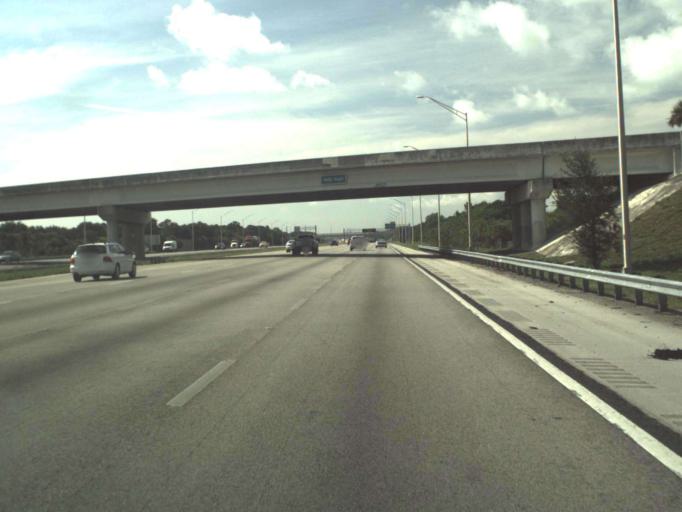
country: US
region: Florida
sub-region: Palm Beach County
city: Palm Beach Gardens
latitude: 26.8655
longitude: -80.1185
